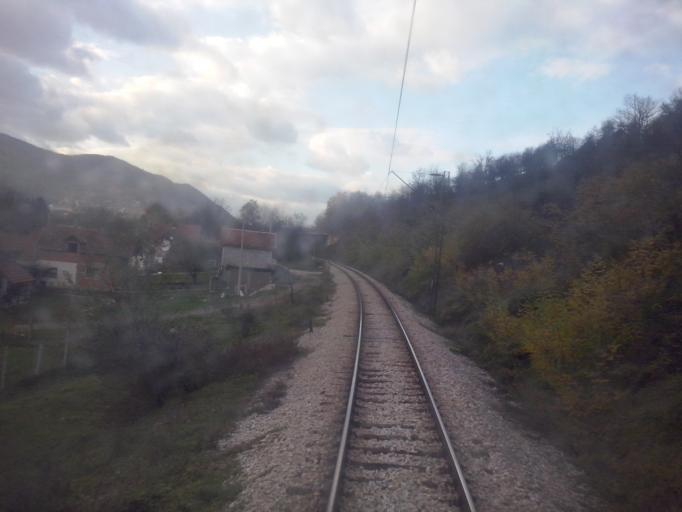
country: RS
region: Central Serbia
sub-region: Zlatiborski Okrug
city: Kosjeric
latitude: 43.9899
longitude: 19.9234
